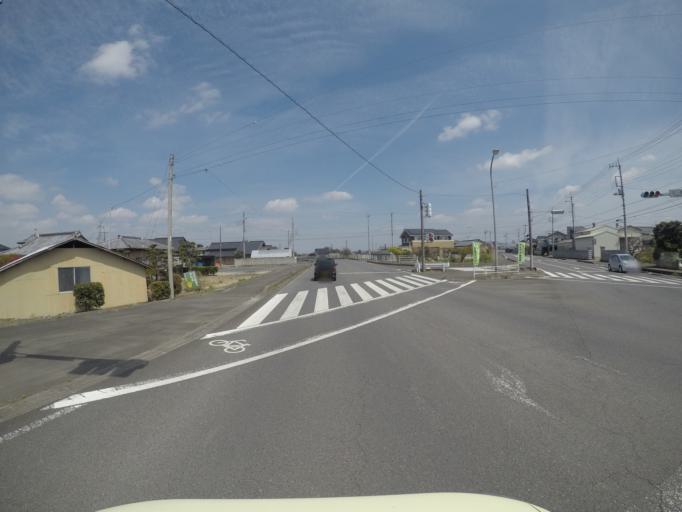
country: JP
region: Ibaraki
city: Shimodate
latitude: 36.3271
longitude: 139.9956
